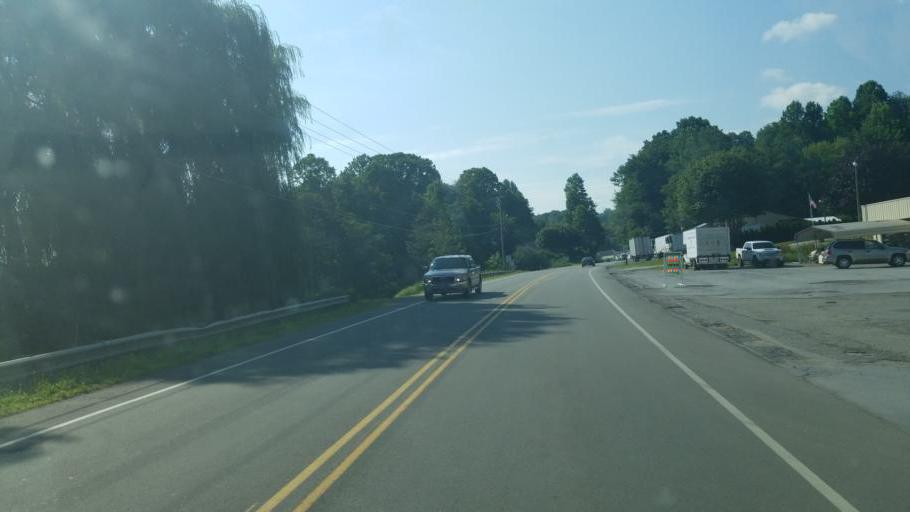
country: US
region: North Carolina
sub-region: Avery County
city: Newland
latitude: 36.1609
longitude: -81.9840
